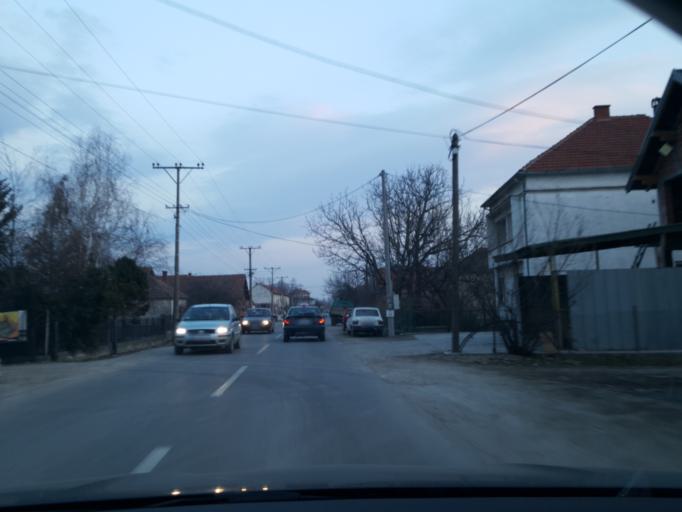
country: RS
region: Central Serbia
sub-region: Nisavski Okrug
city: Aleksinac
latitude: 43.5024
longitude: 21.7011
